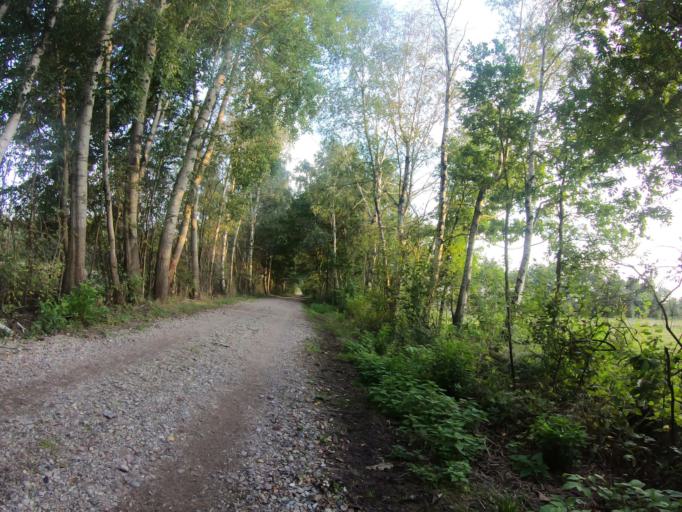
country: DE
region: Lower Saxony
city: Wagenhoff
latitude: 52.5472
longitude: 10.5303
